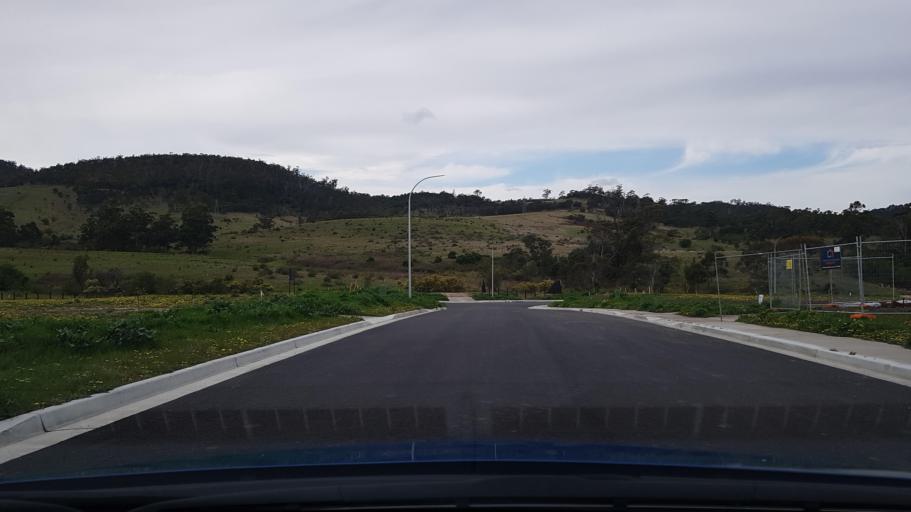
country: AU
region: Tasmania
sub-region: Clarence
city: Rokeby
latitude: -42.8774
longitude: 147.4317
